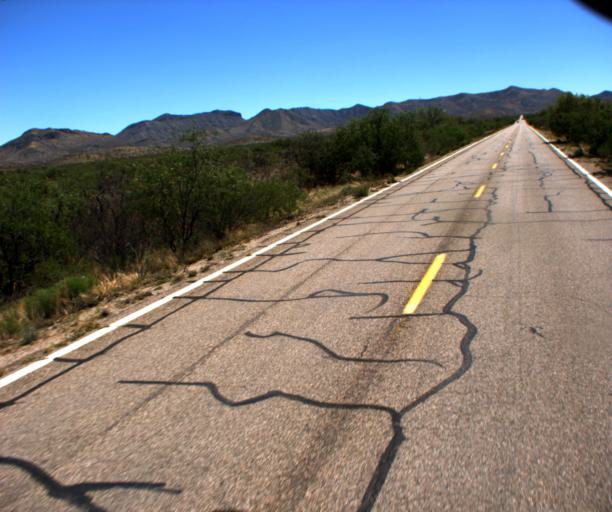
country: US
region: Arizona
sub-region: Pima County
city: Vail
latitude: 31.9556
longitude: -110.6689
